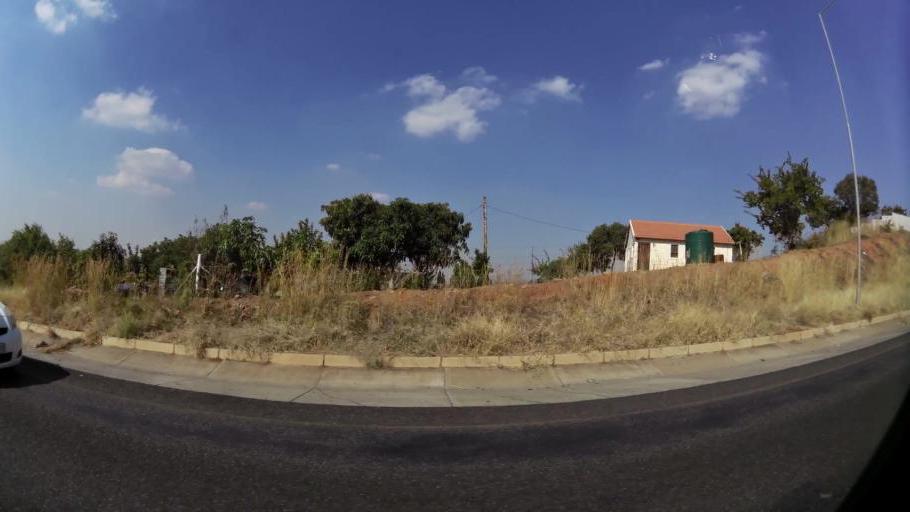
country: ZA
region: North-West
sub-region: Bojanala Platinum District Municipality
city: Rustenburg
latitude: -25.5864
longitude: 27.1289
